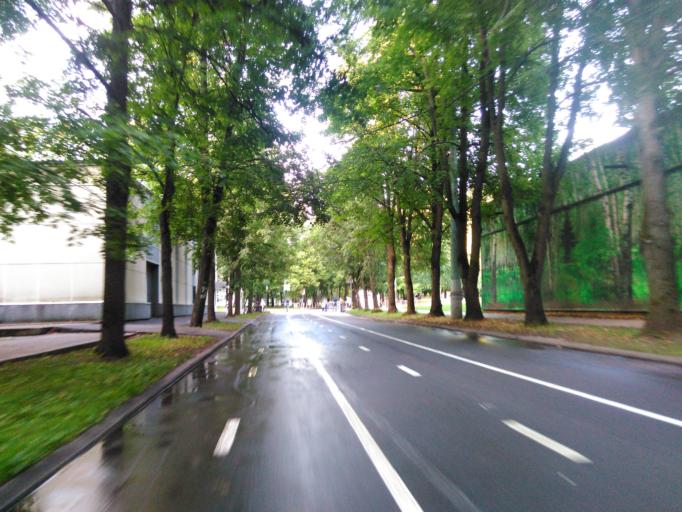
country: RU
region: Moscow
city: Sokol'niki
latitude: 55.7982
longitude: 37.6699
